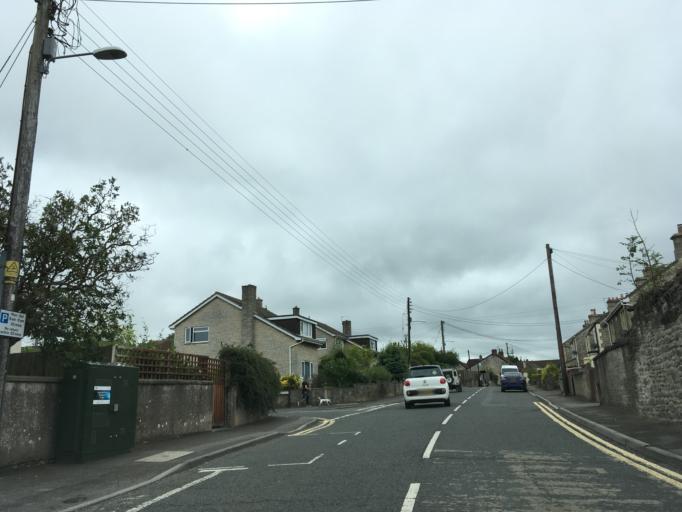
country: GB
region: England
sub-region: Bath and North East Somerset
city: Paulton
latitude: 51.3234
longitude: -2.5100
